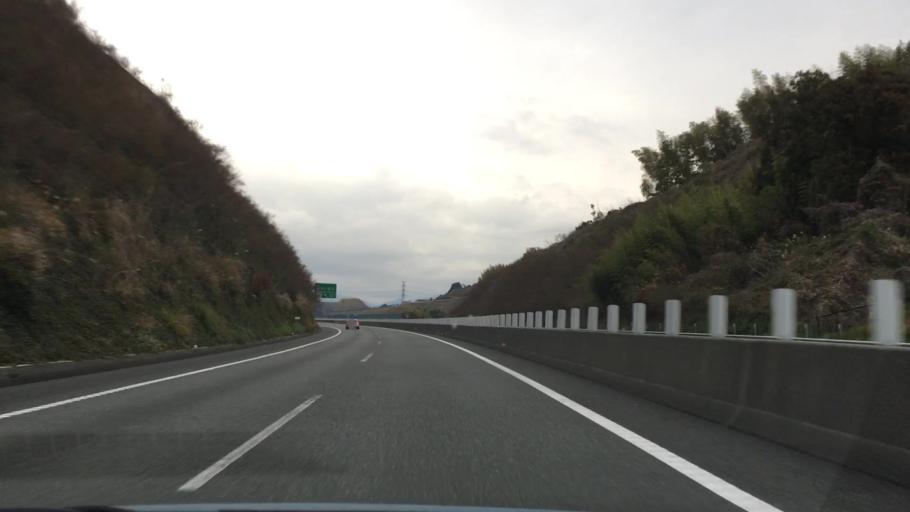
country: JP
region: Shizuoka
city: Shizuoka-shi
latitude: 35.0652
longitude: 138.4805
